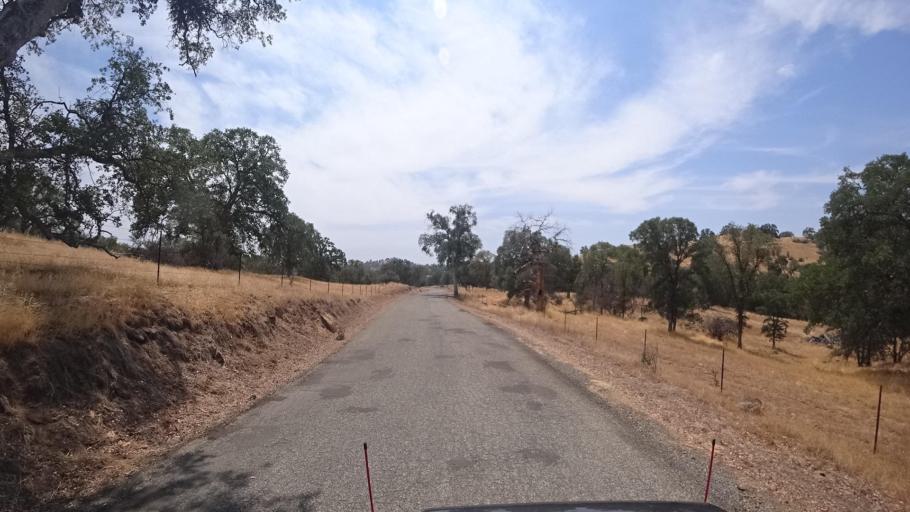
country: US
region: California
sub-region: Mariposa County
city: Mariposa
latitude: 37.3851
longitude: -119.8725
